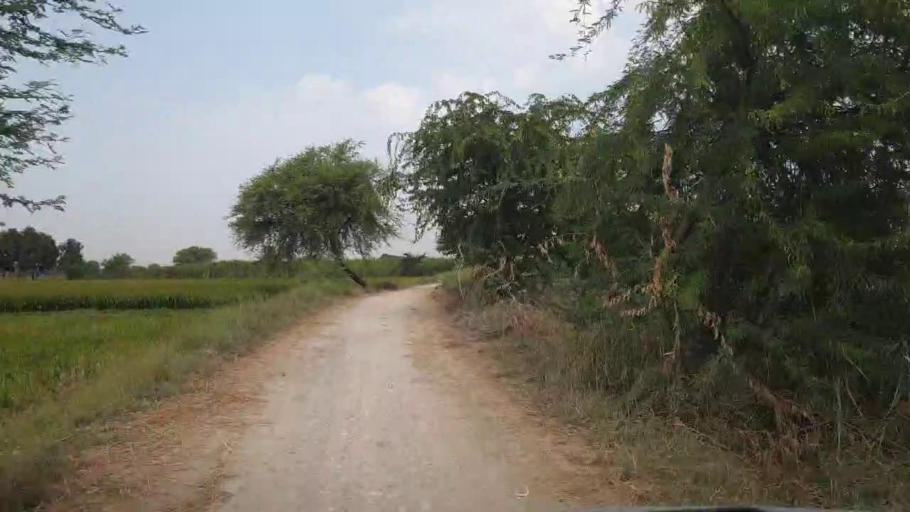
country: PK
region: Sindh
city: Matli
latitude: 24.9590
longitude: 68.7153
